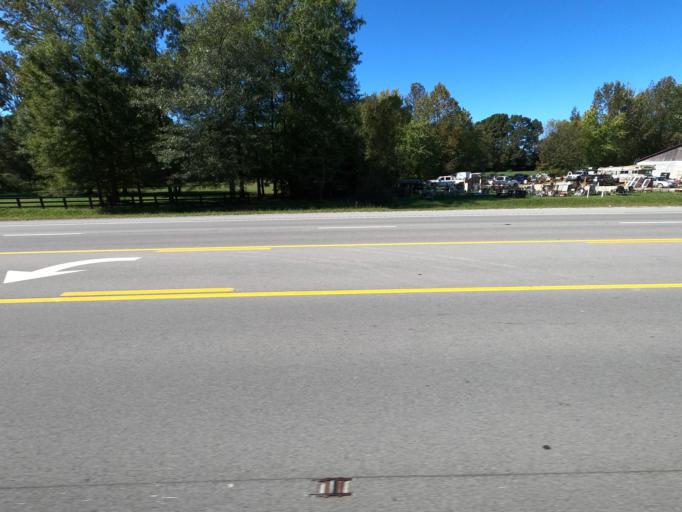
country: US
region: Tennessee
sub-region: Maury County
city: Mount Pleasant
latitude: 35.4364
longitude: -87.2800
